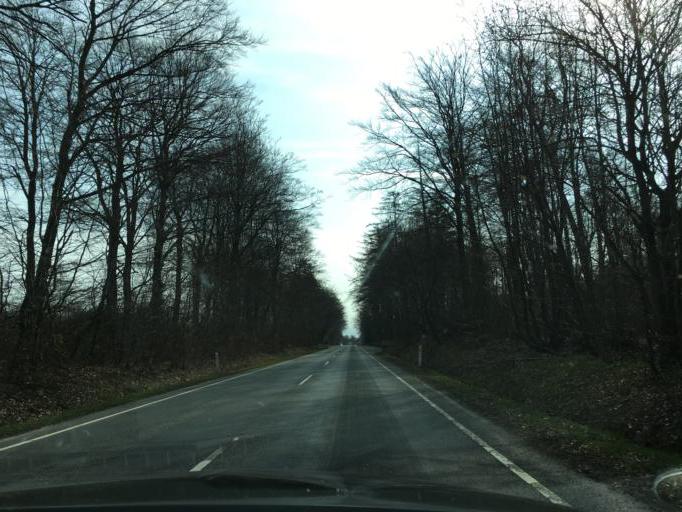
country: DK
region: South Denmark
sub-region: Vejen Kommune
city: Vejen
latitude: 55.4926
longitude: 9.0828
